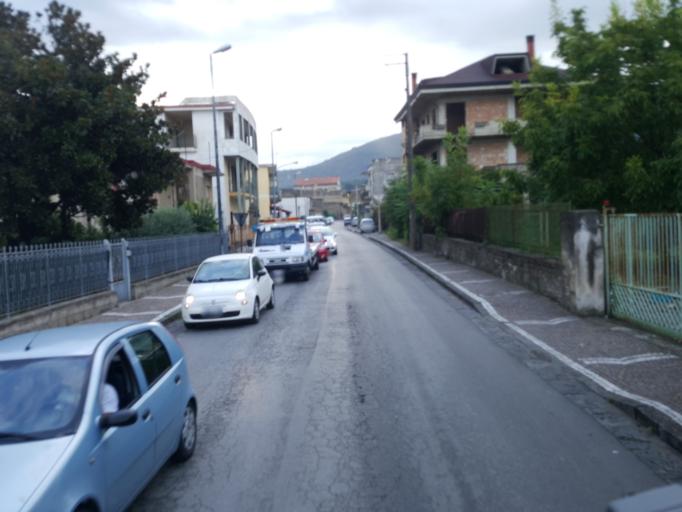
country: IT
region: Campania
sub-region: Provincia di Napoli
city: Palma Campania
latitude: 40.8799
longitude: 14.5510
